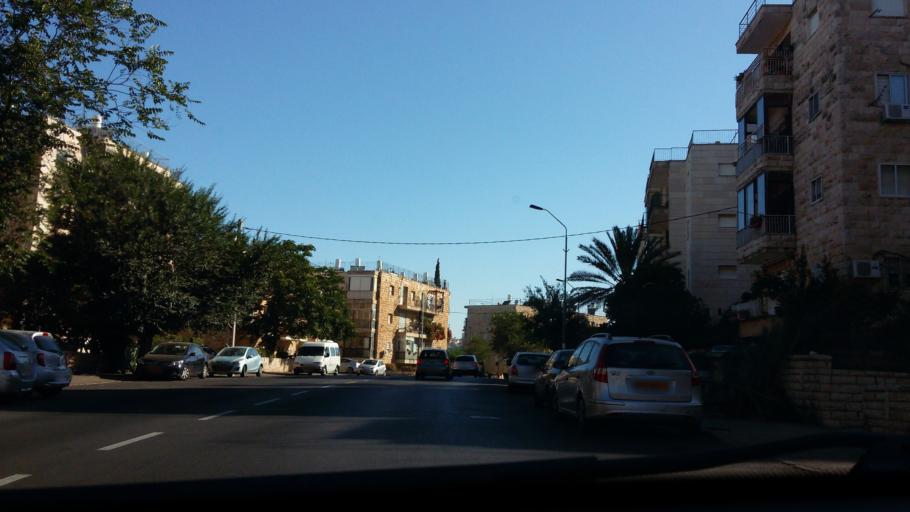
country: IL
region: Jerusalem
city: Jerusalem
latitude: 31.7671
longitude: 35.2060
